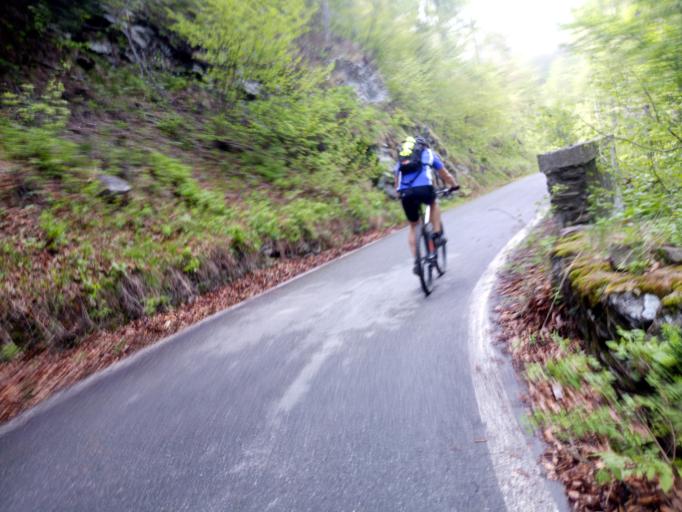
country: IT
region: Piedmont
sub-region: Provincia di Torino
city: Meana di Susa
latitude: 45.1033
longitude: 7.0652
